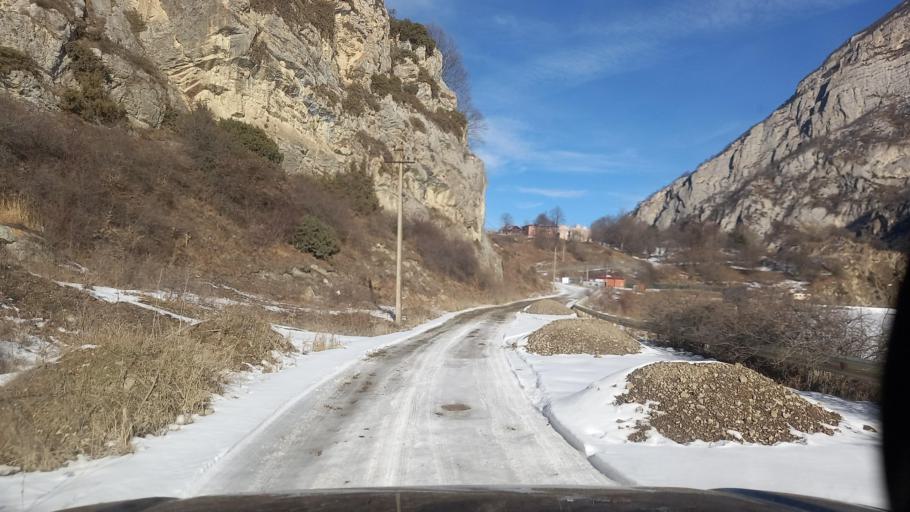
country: RU
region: North Ossetia
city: Verkhniy Fiagdon
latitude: 42.8764
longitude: 44.4480
